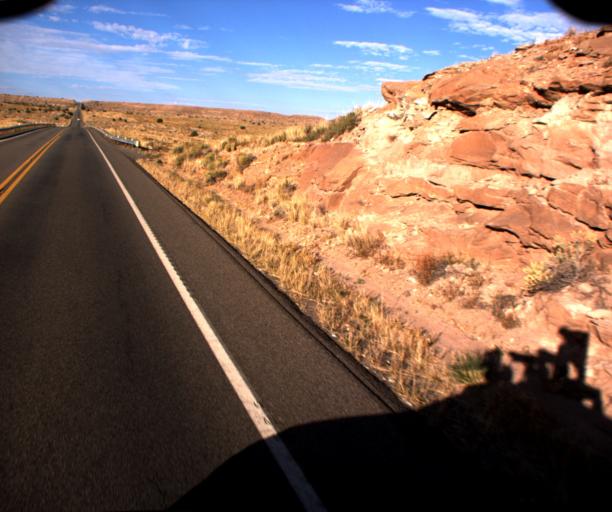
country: US
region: New Mexico
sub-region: San Juan County
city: Shiprock
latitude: 36.9344
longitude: -109.1325
